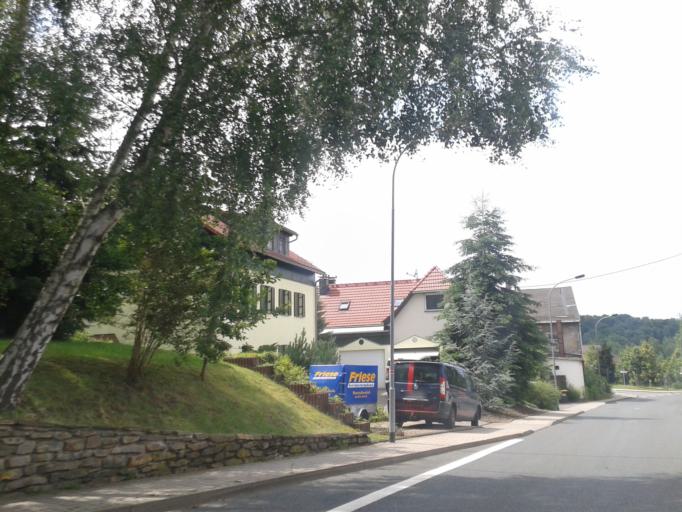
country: DE
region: Saxony
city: Halsbrucke
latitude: 50.9556
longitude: 13.3530
